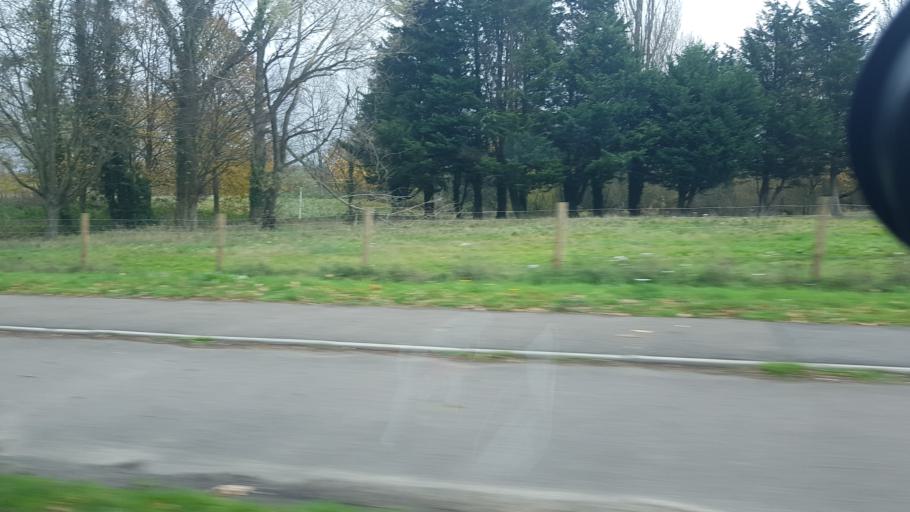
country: GB
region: England
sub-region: Hampshire
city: Farnborough
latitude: 51.2868
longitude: -0.7787
